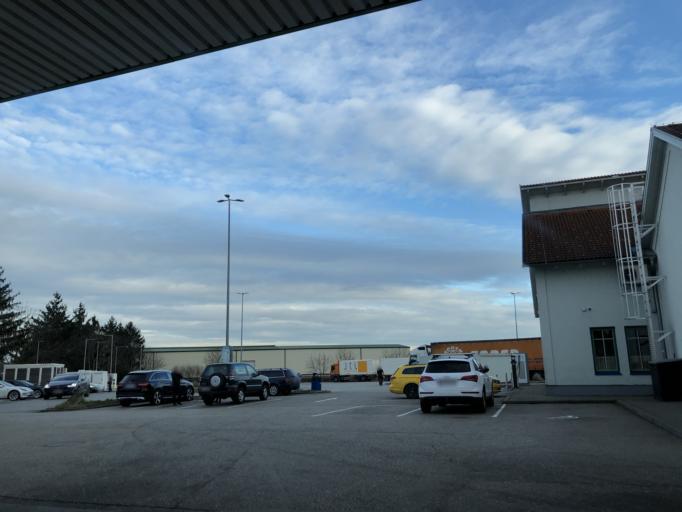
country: AT
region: Lower Austria
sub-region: Politischer Bezirk Amstetten
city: Ennsdorf
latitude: 48.1968
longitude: 14.5272
